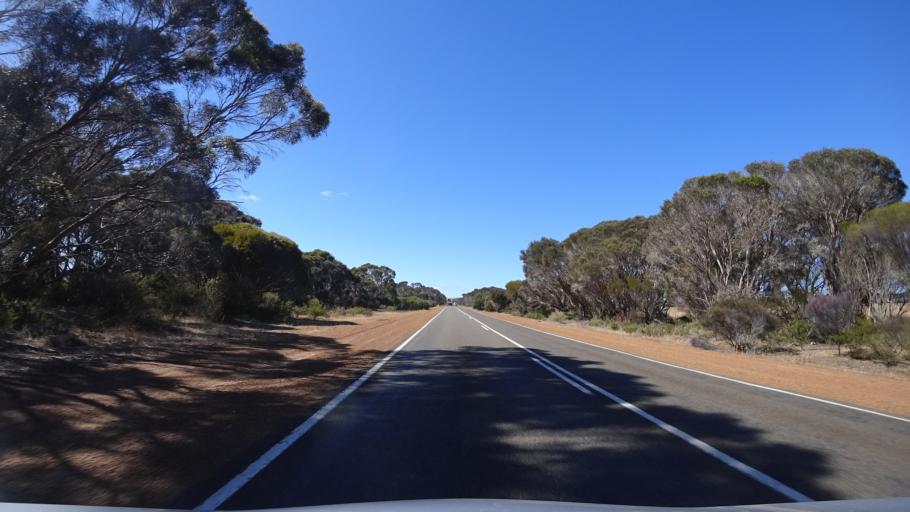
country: AU
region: South Australia
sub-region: Kangaroo Island
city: Kingscote
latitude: -35.7191
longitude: 137.5596
